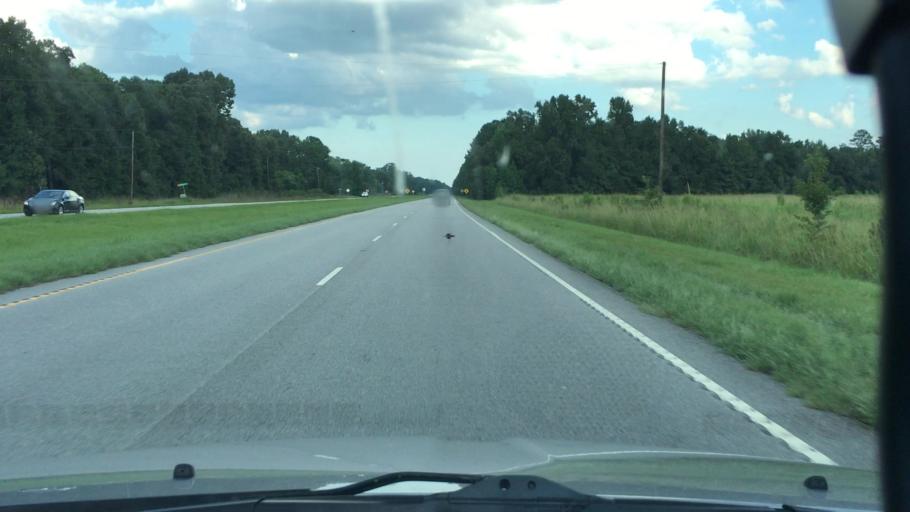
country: US
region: South Carolina
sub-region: Hampton County
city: Yemassee
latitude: 32.6363
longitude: -80.8436
